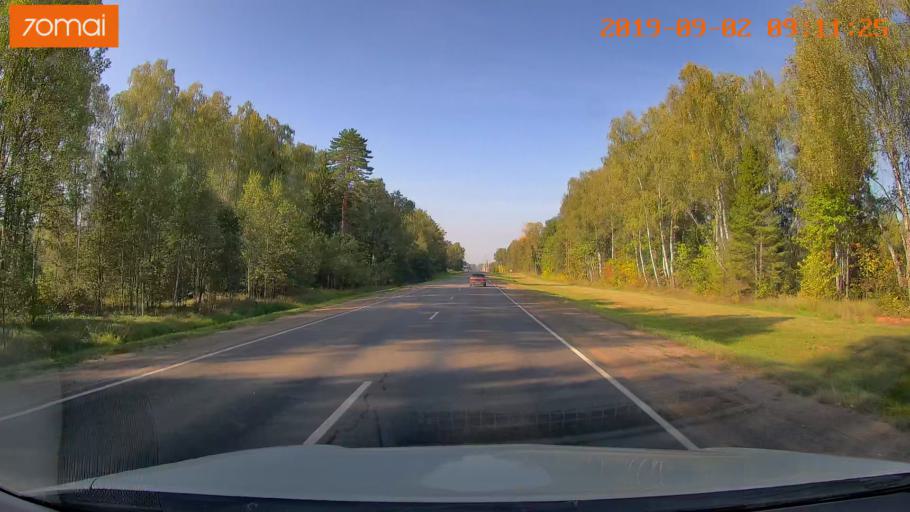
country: RU
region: Kaluga
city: Myatlevo
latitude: 54.8677
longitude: 35.5763
